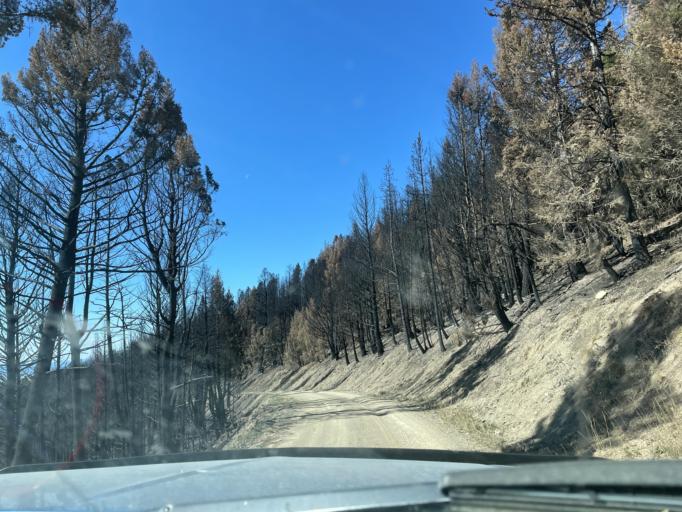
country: US
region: Montana
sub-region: Broadwater County
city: Townsend
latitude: 46.5070
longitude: -111.2764
